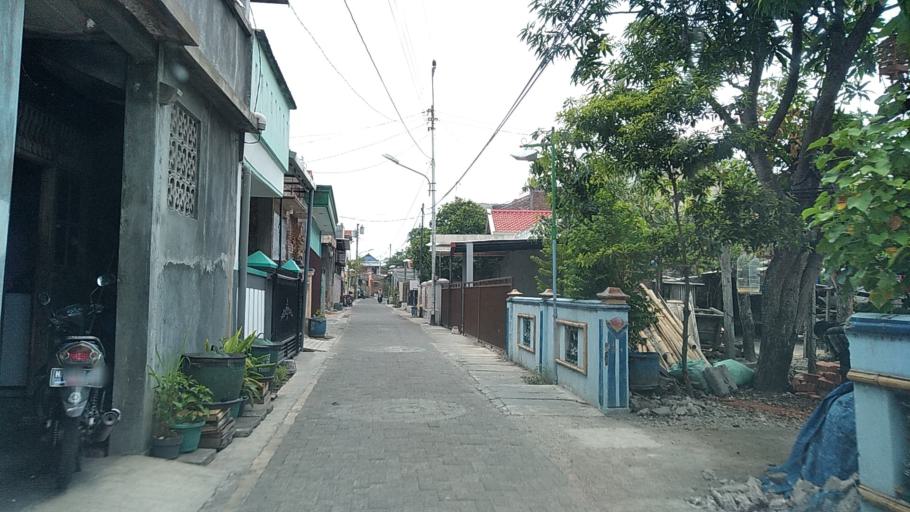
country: ID
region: Central Java
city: Mranggen
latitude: -7.0153
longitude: 110.4678
